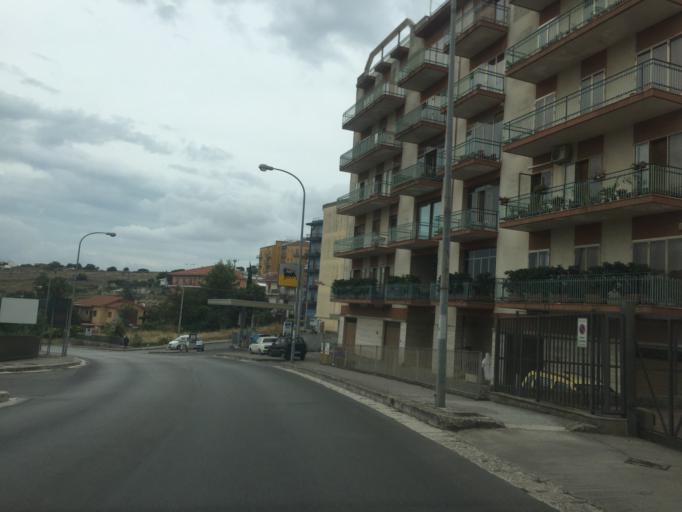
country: IT
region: Sicily
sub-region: Ragusa
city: Ragusa
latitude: 36.9177
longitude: 14.7313
